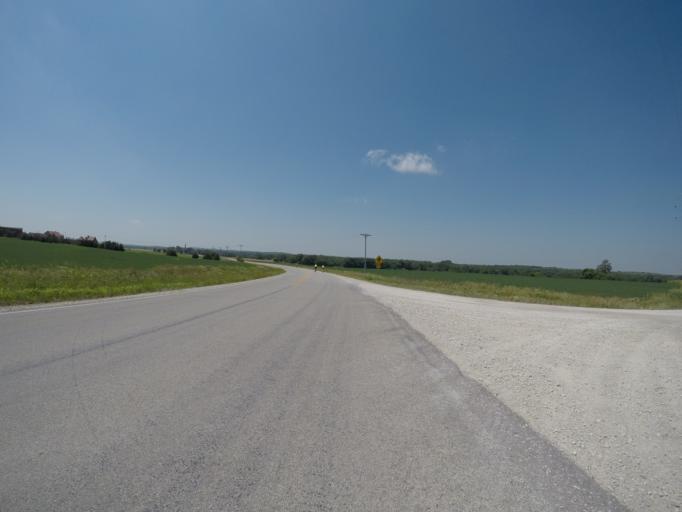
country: US
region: Kansas
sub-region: Pottawatomie County
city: Westmoreland
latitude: 39.3050
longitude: -96.4403
